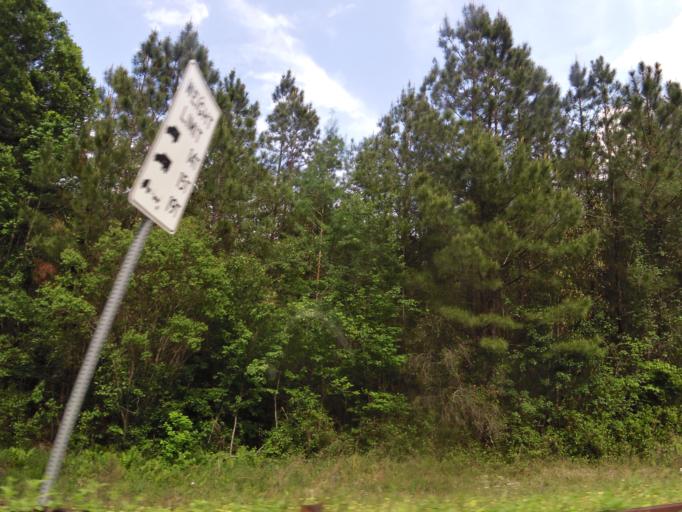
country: US
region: Georgia
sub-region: Charlton County
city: Folkston
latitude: 30.8127
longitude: -82.0693
